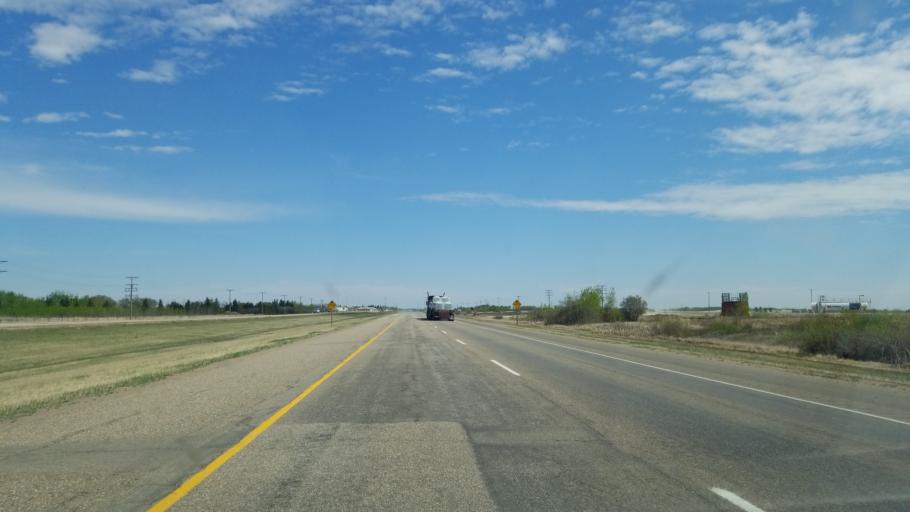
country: CA
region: Saskatchewan
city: Lloydminster
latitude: 53.1356
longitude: -109.6446
